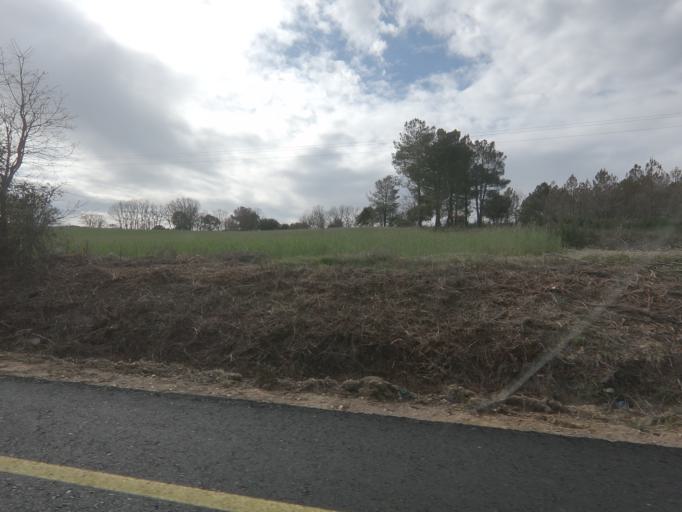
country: ES
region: Castille and Leon
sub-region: Provincia de Salamanca
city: Robleda
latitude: 40.3651
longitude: -6.6212
